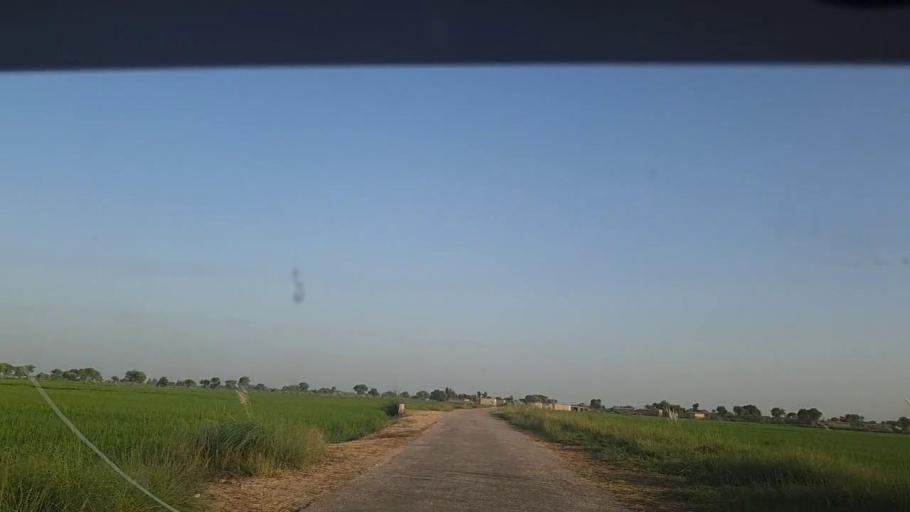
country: PK
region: Sindh
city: Thul
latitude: 28.1338
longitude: 68.8897
